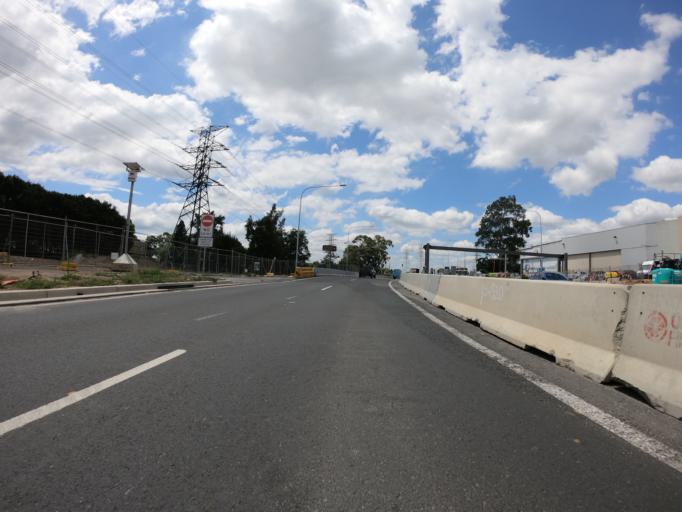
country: AU
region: New South Wales
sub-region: Penrith Municipality
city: Penrith
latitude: -33.7479
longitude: 150.6889
